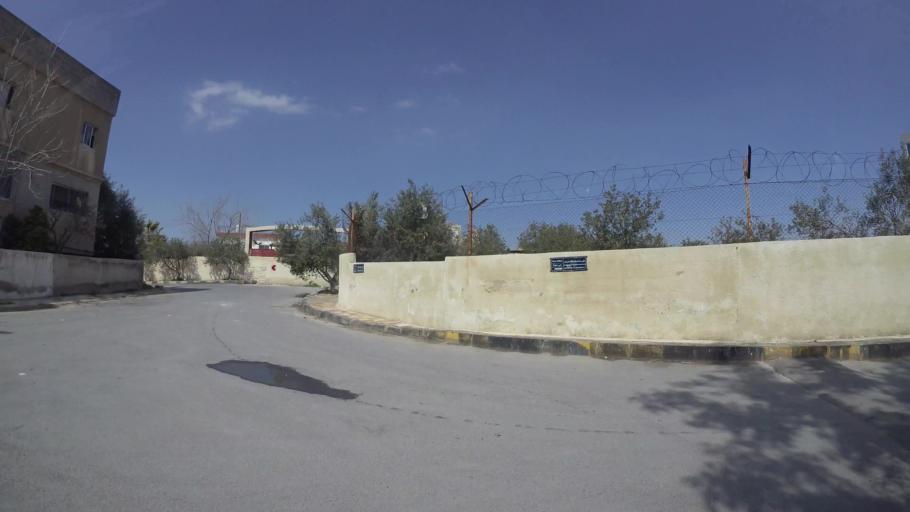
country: JO
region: Zarqa
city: Russeifa
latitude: 31.9955
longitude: 35.9976
